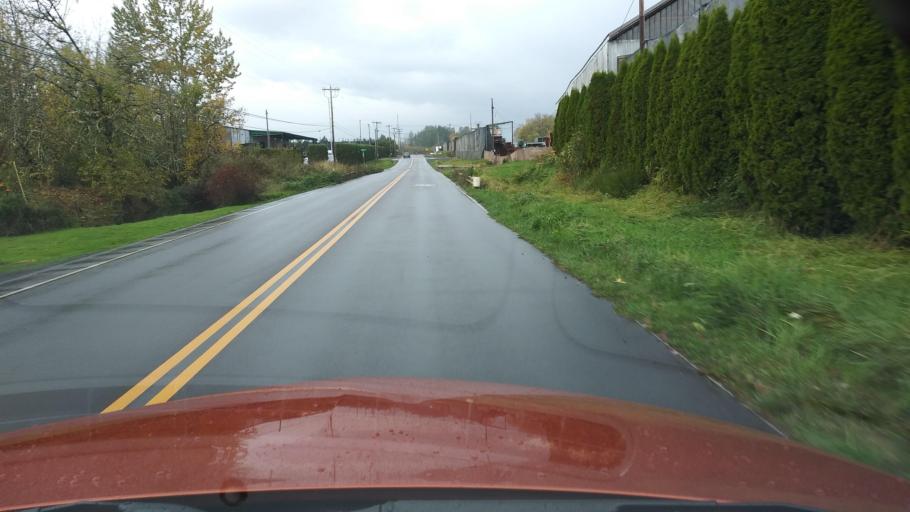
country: US
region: Oregon
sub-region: Washington County
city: North Plains
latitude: 45.5985
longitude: -123.0081
